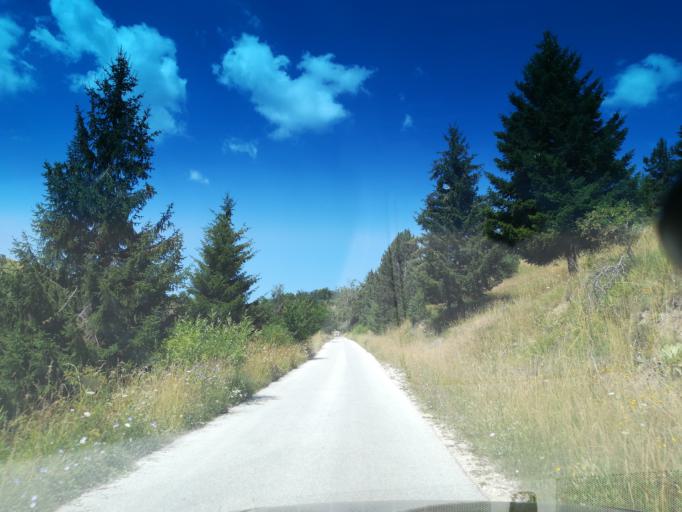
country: BG
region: Smolyan
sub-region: Obshtina Chepelare
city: Chepelare
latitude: 41.6701
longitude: 24.7831
